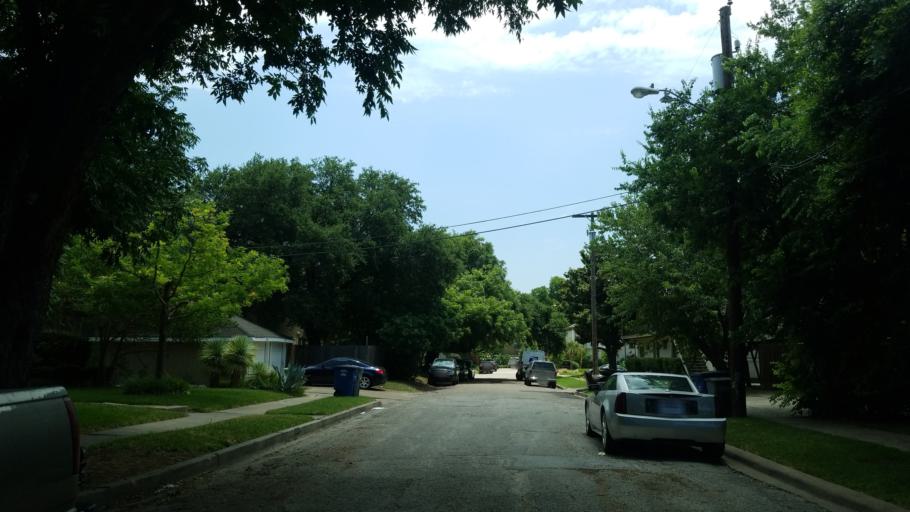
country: US
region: Texas
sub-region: Dallas County
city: Highland Park
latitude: 32.8307
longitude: -96.7669
